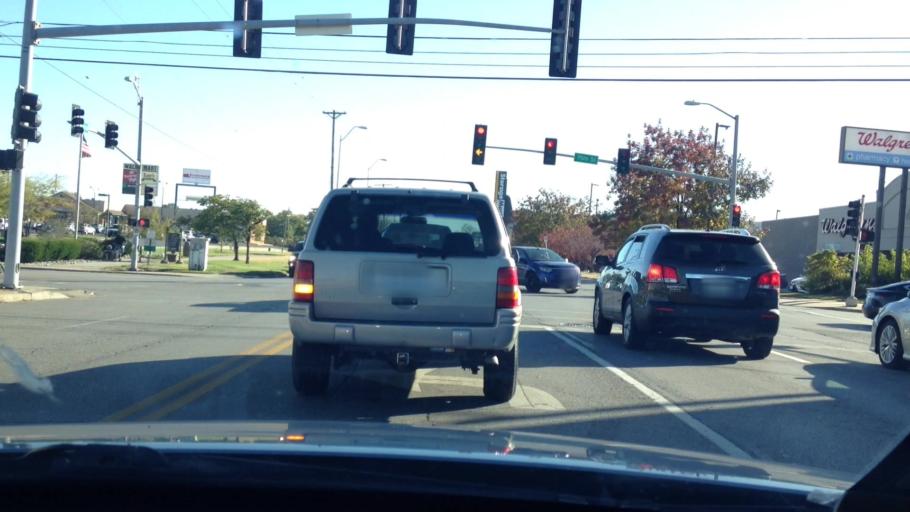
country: US
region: Kansas
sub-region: Johnson County
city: Mission Hills
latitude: 38.9927
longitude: -94.5943
